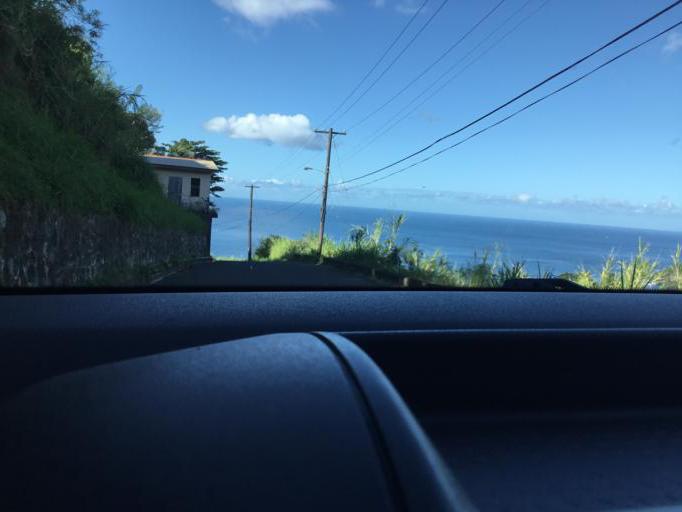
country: VC
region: Saint David
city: Chateaubelair
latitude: 13.2790
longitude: -61.2536
